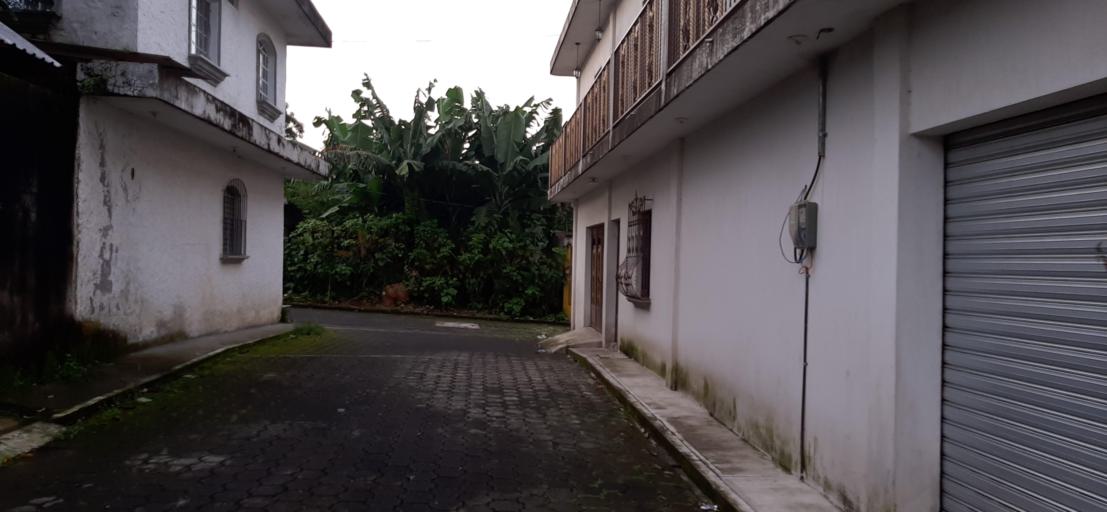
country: GT
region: Retalhuleu
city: San Felipe
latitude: 14.6213
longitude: -91.5986
